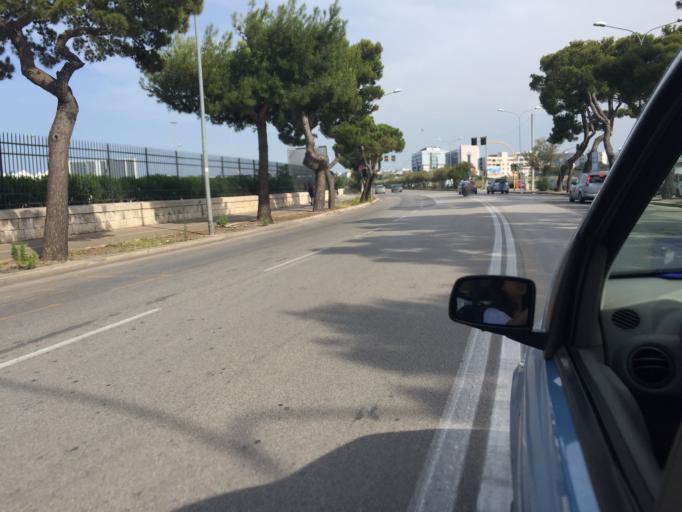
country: IT
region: Apulia
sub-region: Provincia di Bari
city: Bari
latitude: 41.1335
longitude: 16.8446
